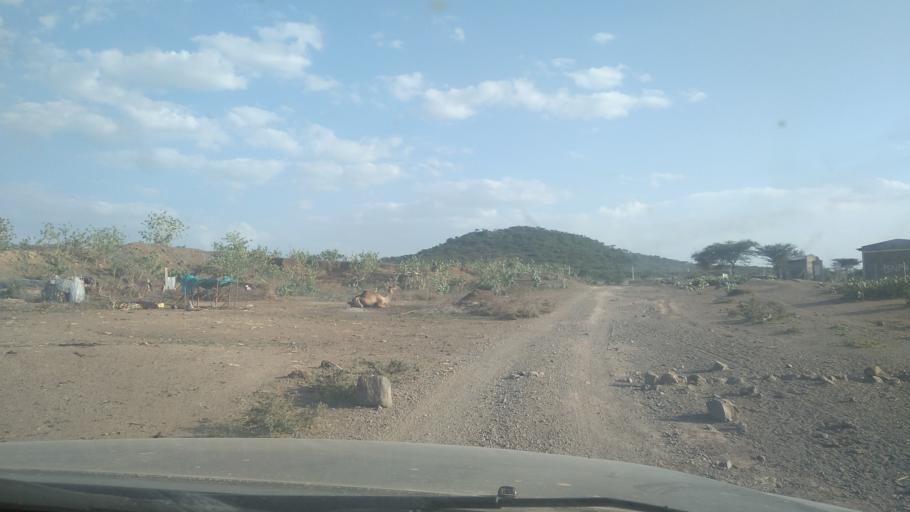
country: ET
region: Oromiya
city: Hirna
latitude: 9.3988
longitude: 40.9475
